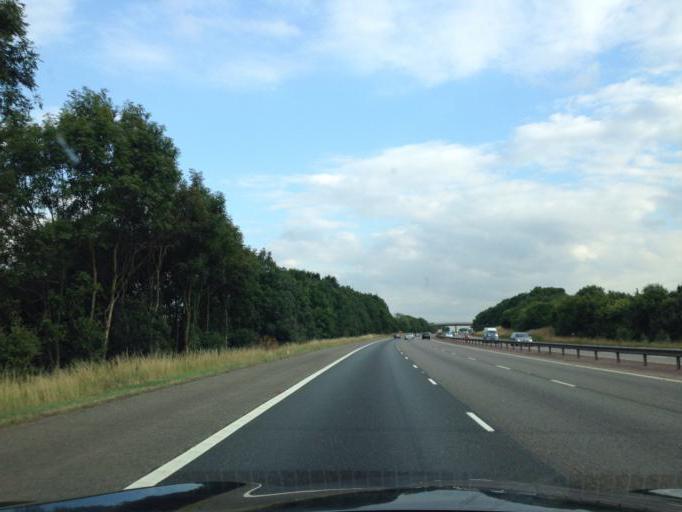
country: GB
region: England
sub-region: Warwickshire
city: Harbury
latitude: 52.1606
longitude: -1.4301
